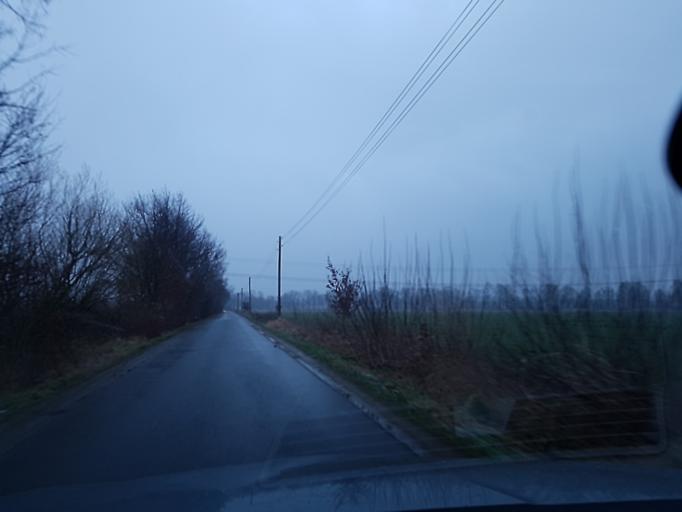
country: DE
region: Brandenburg
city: Groden
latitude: 51.4330
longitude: 13.5562
